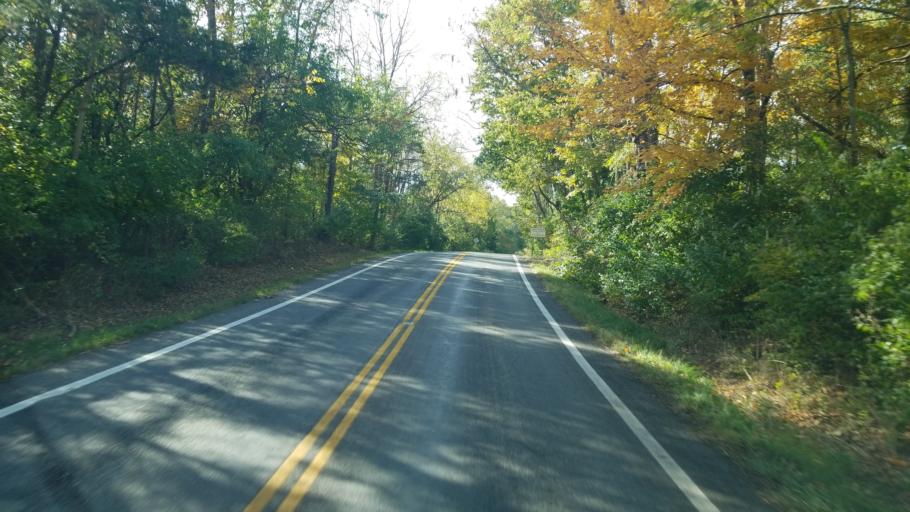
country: US
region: Ohio
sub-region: Warren County
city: Morrow
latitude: 39.4078
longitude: -84.0653
